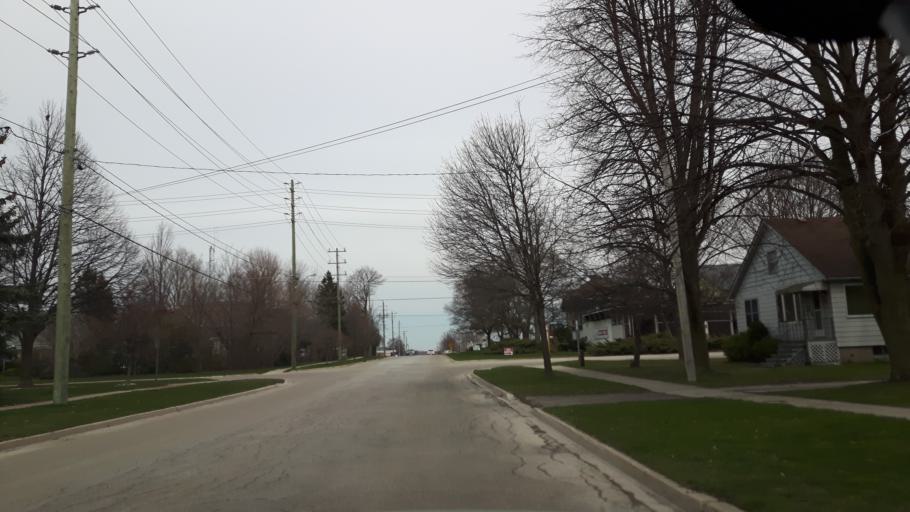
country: CA
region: Ontario
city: Goderich
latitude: 43.7475
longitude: -81.7045
